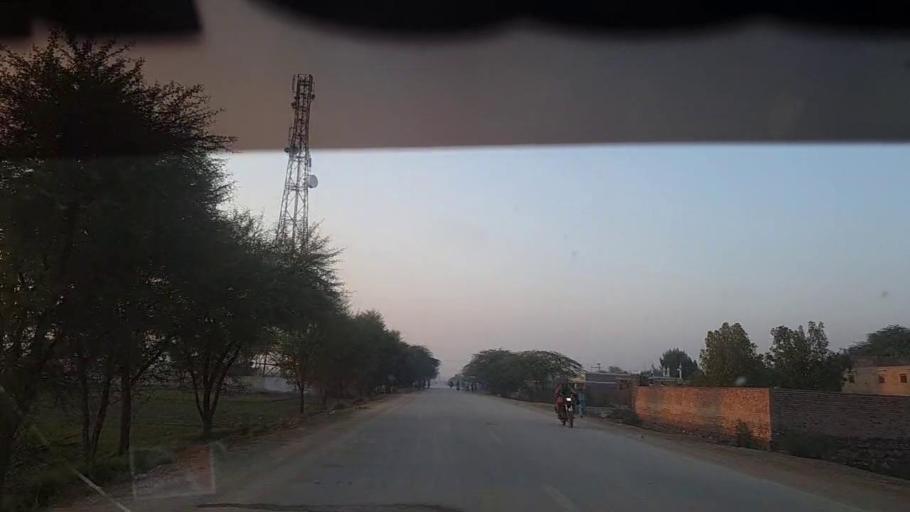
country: PK
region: Sindh
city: Ranipur
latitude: 27.2662
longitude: 68.5214
